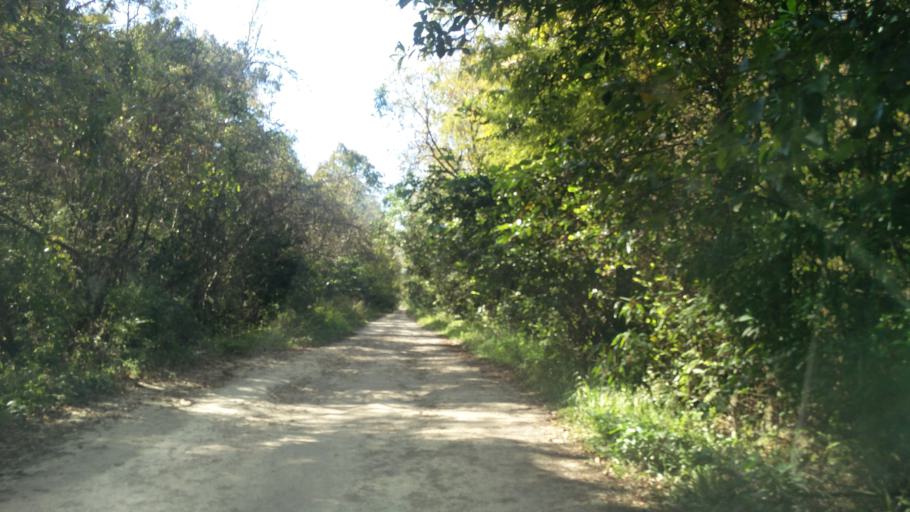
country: US
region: Florida
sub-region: Collier County
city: Lely Resort
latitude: 25.9800
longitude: -81.3965
